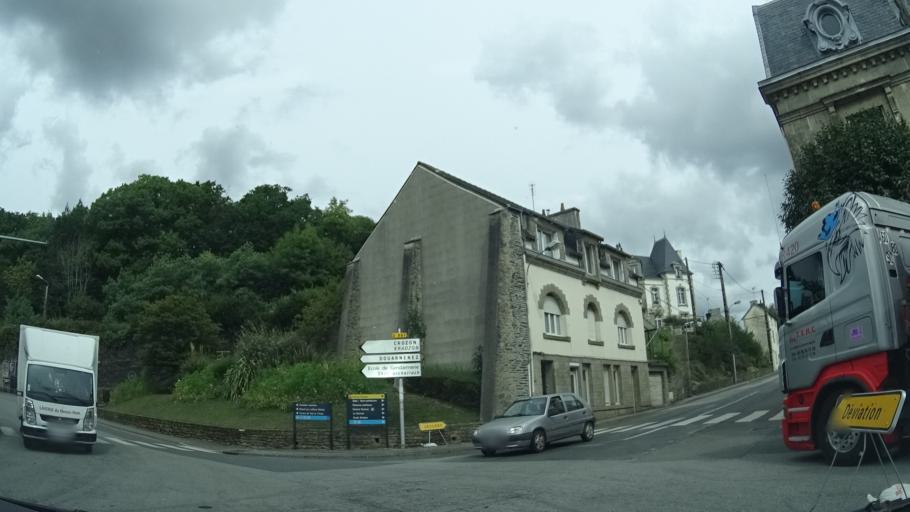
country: FR
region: Brittany
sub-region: Departement du Finistere
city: Chateaulin
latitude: 48.1977
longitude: -4.0918
